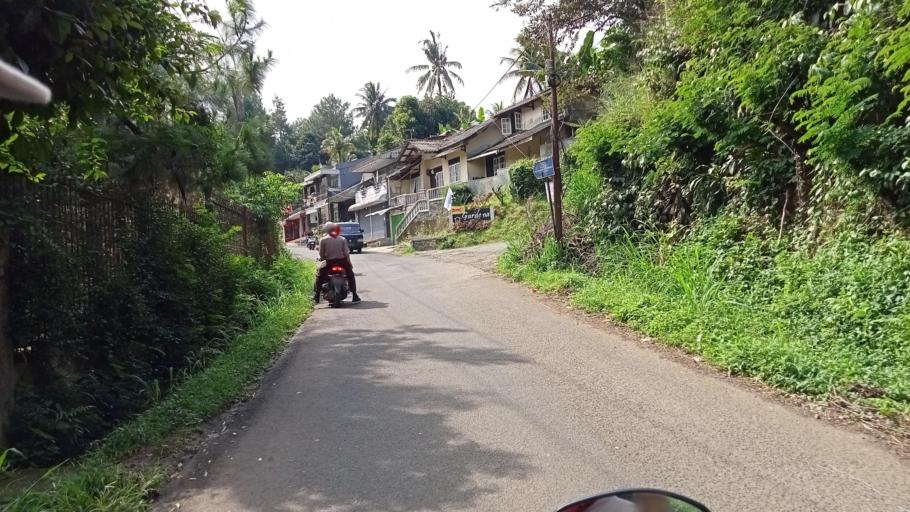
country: ID
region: West Java
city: Caringin
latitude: -6.6467
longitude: 106.9122
